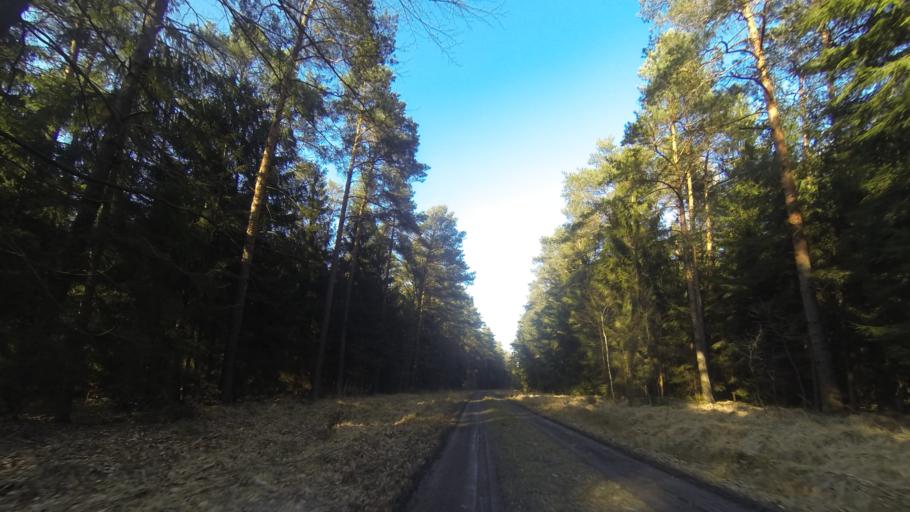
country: DE
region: Saxony
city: Laussnitz
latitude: 51.2557
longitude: 13.8451
